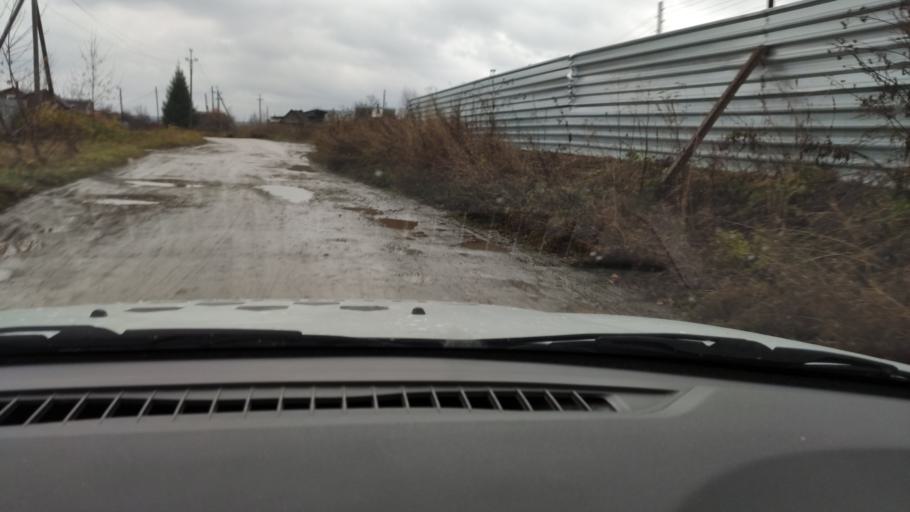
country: RU
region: Perm
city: Sylva
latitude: 58.0449
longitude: 56.7430
